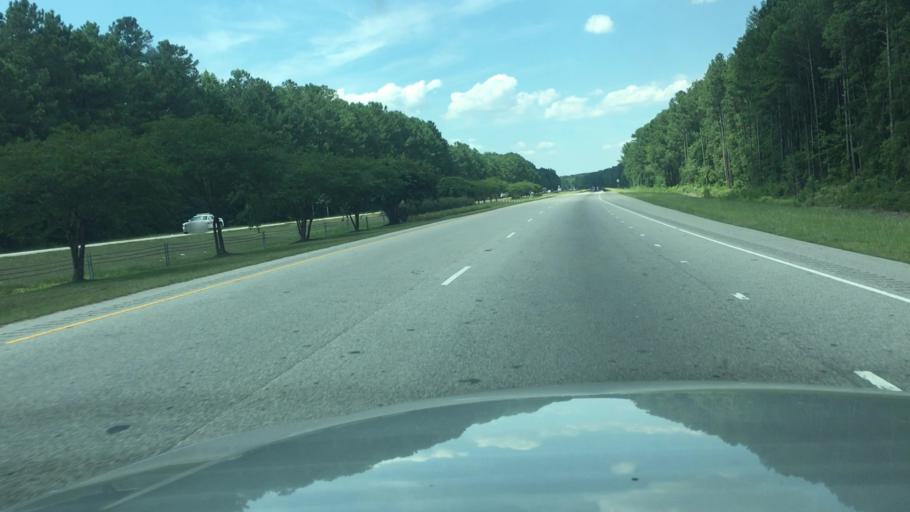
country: US
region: North Carolina
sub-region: Cumberland County
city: Fayetteville
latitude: 34.9843
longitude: -78.8603
